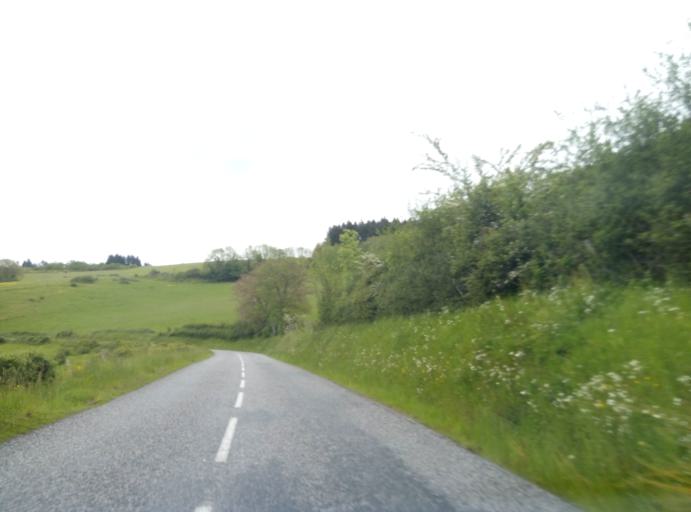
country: FR
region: Rhone-Alpes
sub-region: Departement du Rhone
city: Tarare
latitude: 45.9178
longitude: 4.4303
